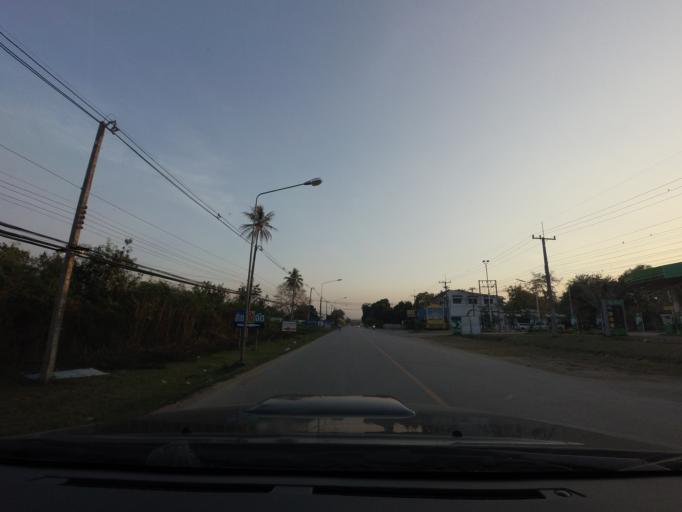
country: TH
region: Chiang Mai
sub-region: Amphoe Chiang Dao
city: Chiang Dao
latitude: 19.3612
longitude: 98.9645
